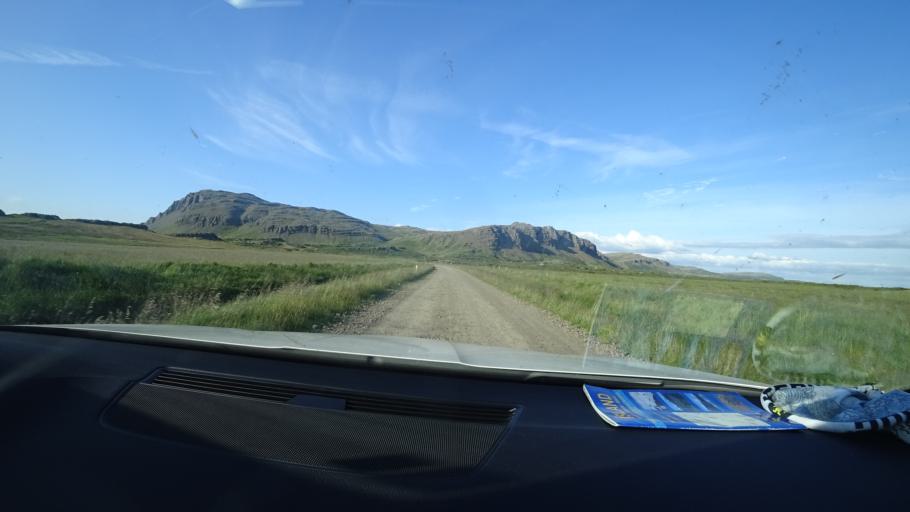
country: IS
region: West
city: Borgarnes
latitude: 64.6872
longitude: -21.9429
